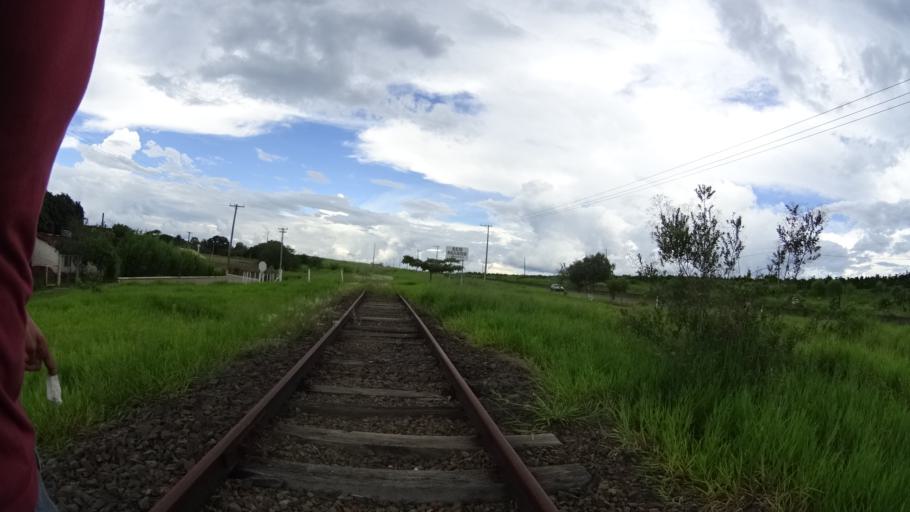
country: BR
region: Sao Paulo
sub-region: Marilia
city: Marilia
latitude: -22.2182
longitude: -49.8627
